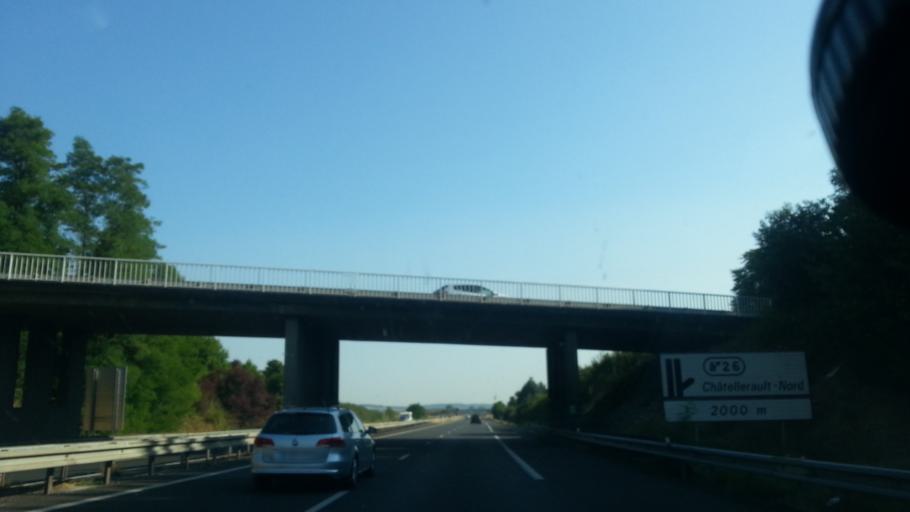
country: FR
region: Poitou-Charentes
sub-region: Departement de la Vienne
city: Chatellerault
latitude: 46.8194
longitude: 0.5165
